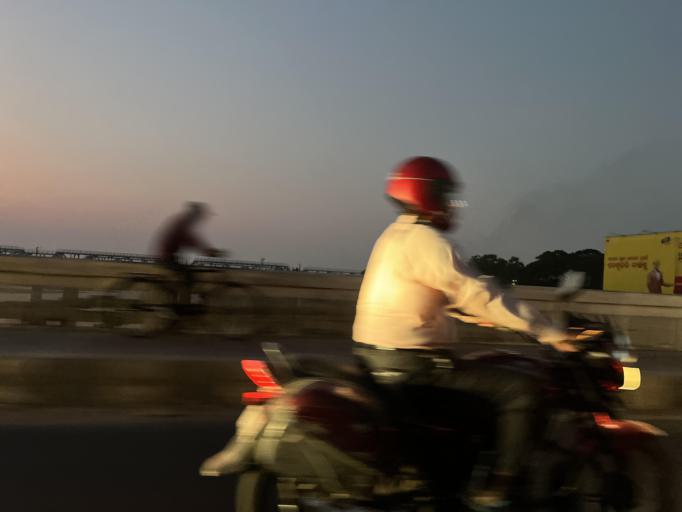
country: IN
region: Odisha
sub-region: Cuttack
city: Cuttack
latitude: 20.4426
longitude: 85.8926
